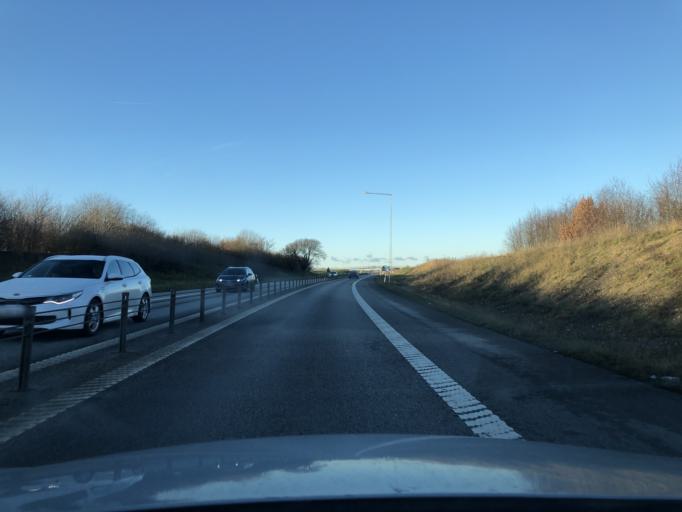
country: SE
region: Skane
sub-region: Trelleborgs Kommun
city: Skare
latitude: 55.3795
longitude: 13.0909
